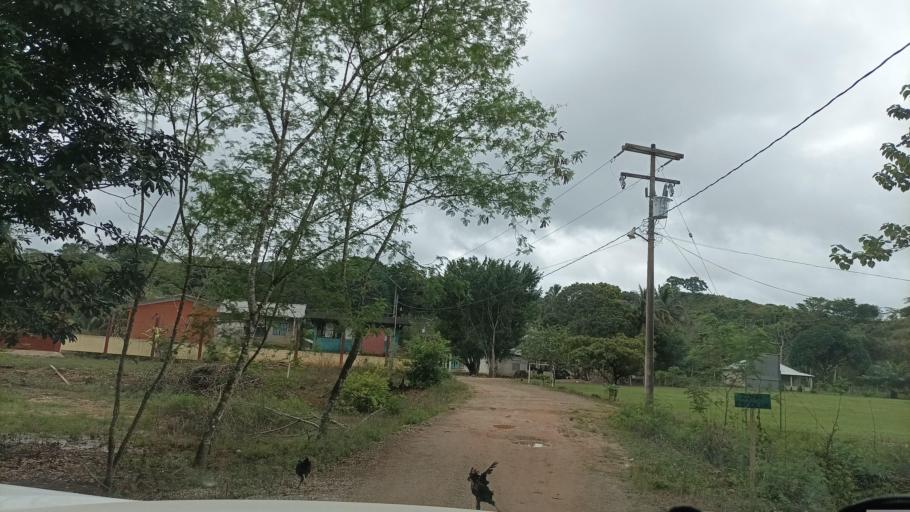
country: MX
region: Veracruz
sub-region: Uxpanapa
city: Poblado 10
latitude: 17.4288
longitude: -94.4214
